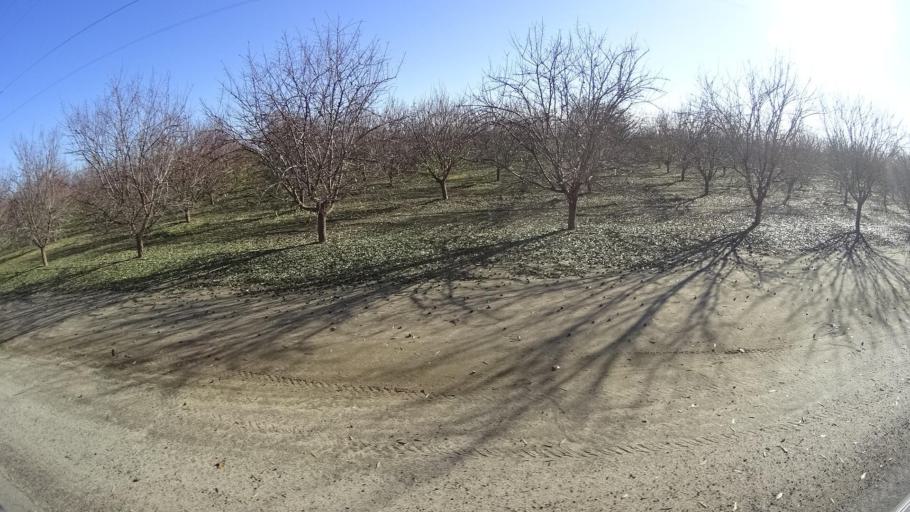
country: US
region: California
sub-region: Kern County
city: Delano
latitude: 35.7349
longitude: -119.3119
